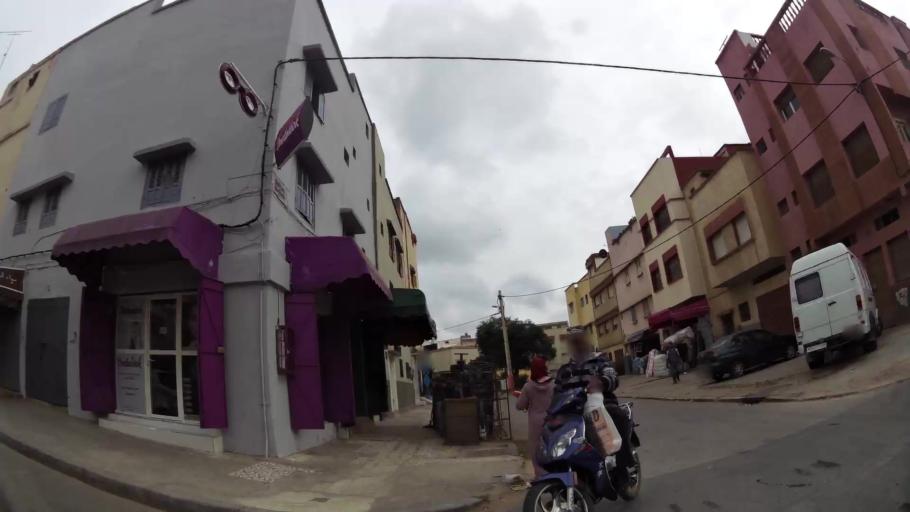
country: MA
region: Rabat-Sale-Zemmour-Zaer
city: Sale
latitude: 34.0481
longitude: -6.7961
